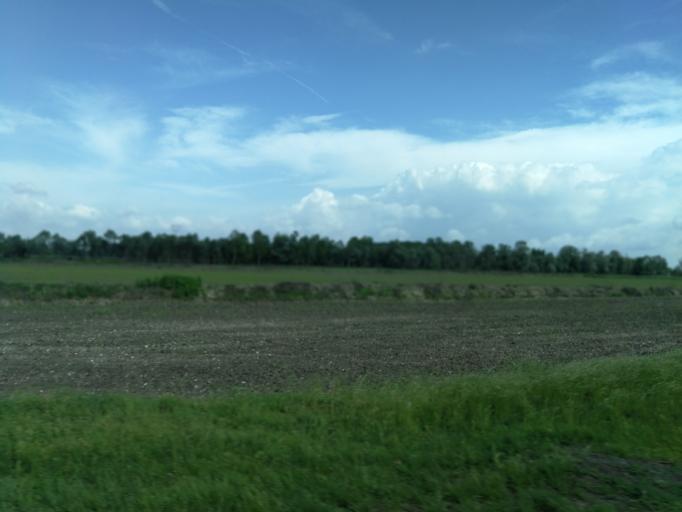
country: IT
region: Piedmont
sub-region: Provincia di Cuneo
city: Faule
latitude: 44.8157
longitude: 7.5861
